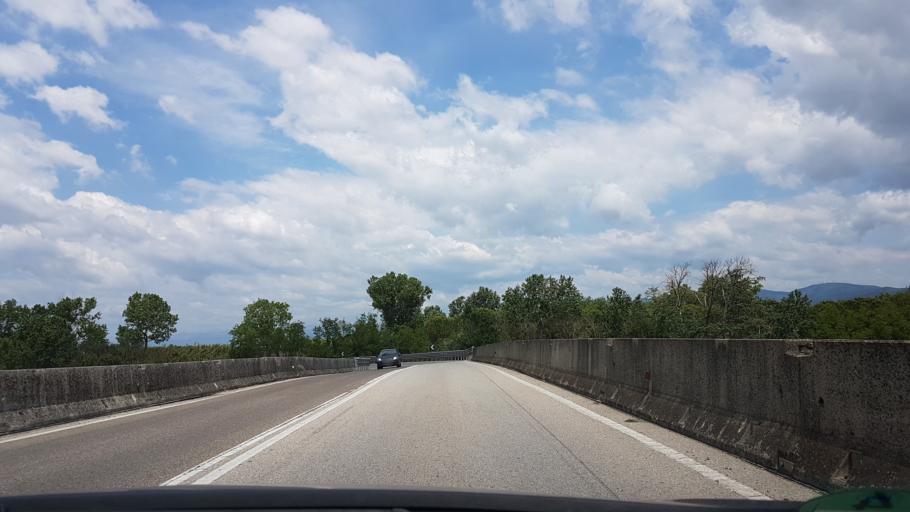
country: IT
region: Tuscany
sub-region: Provincia di Livorno
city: Vicarello
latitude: 43.6230
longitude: 10.4663
